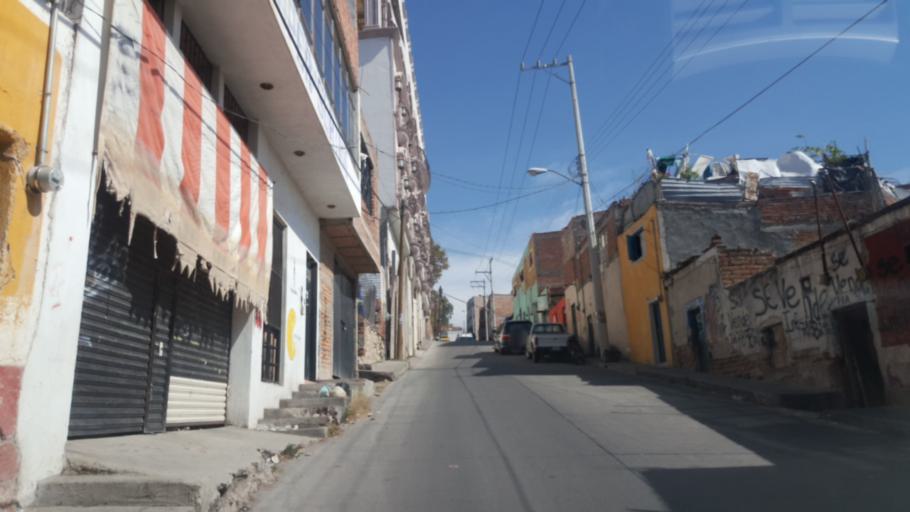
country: MX
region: Jalisco
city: San Juan de los Lagos
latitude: 21.2498
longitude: -102.3335
